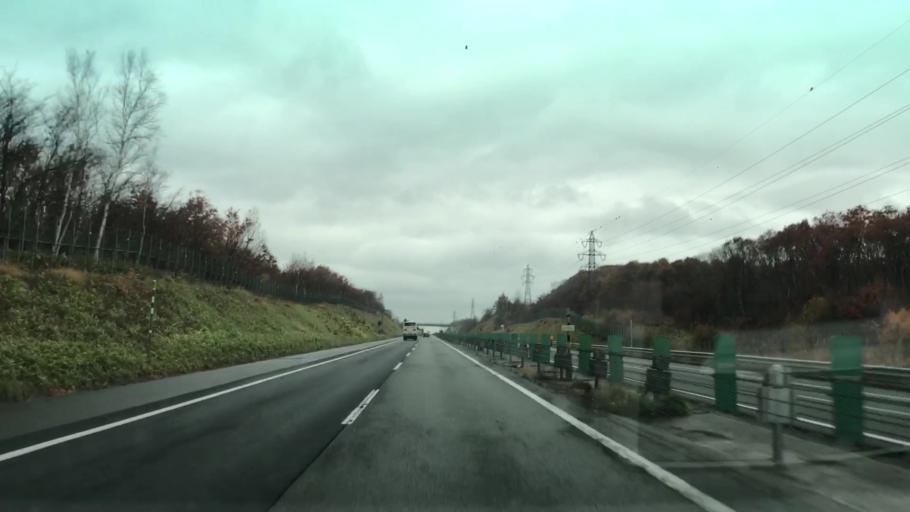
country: JP
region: Hokkaido
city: Kitahiroshima
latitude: 42.9594
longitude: 141.5021
